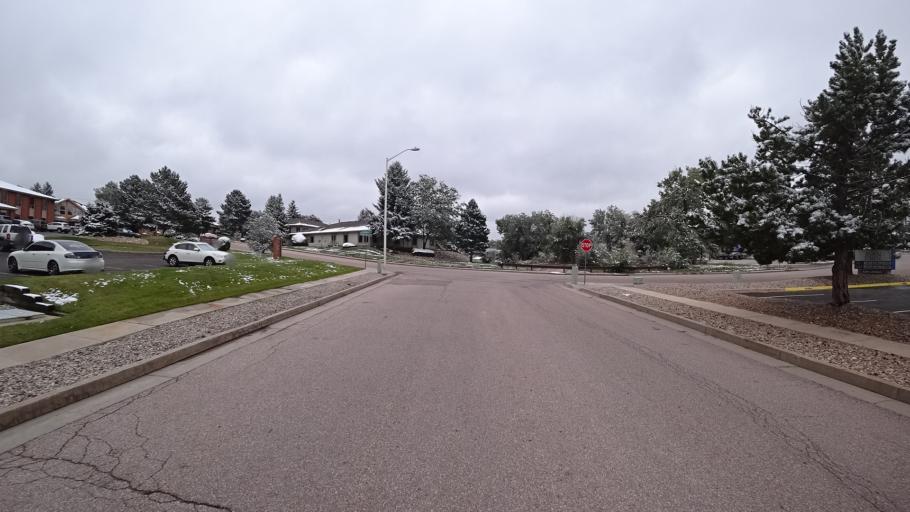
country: US
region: Colorado
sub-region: El Paso County
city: Colorado Springs
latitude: 38.9219
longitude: -104.7895
